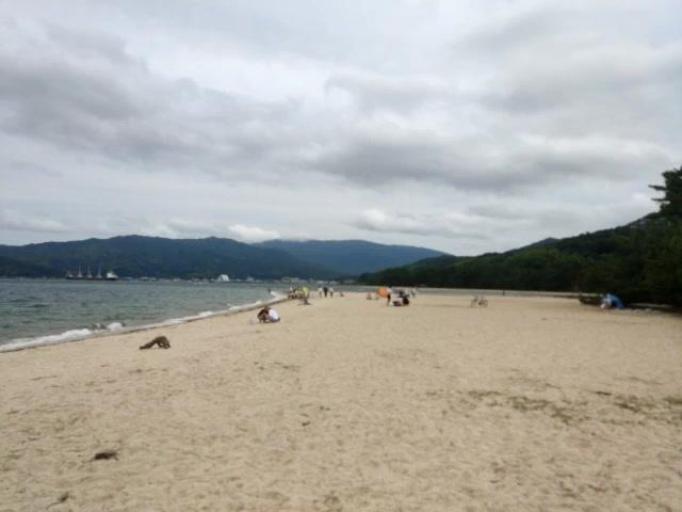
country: JP
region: Kyoto
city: Miyazu
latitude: 35.5600
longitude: 135.1875
